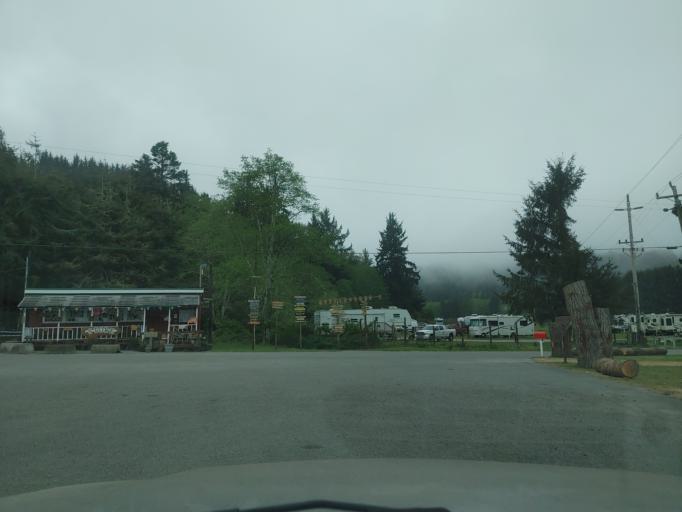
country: US
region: California
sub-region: Humboldt County
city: Westhaven-Moonstone
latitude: 41.2241
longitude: -124.0880
